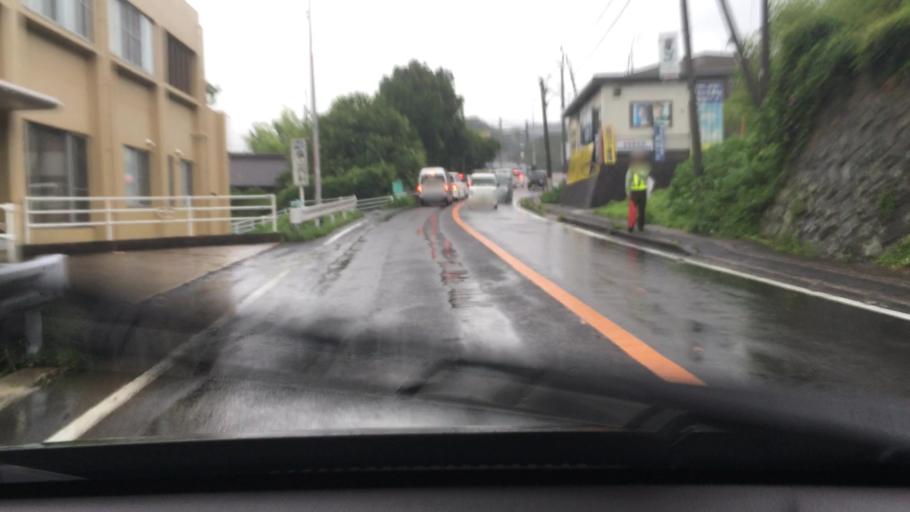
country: JP
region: Nagasaki
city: Sasebo
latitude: 33.1401
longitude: 129.7958
